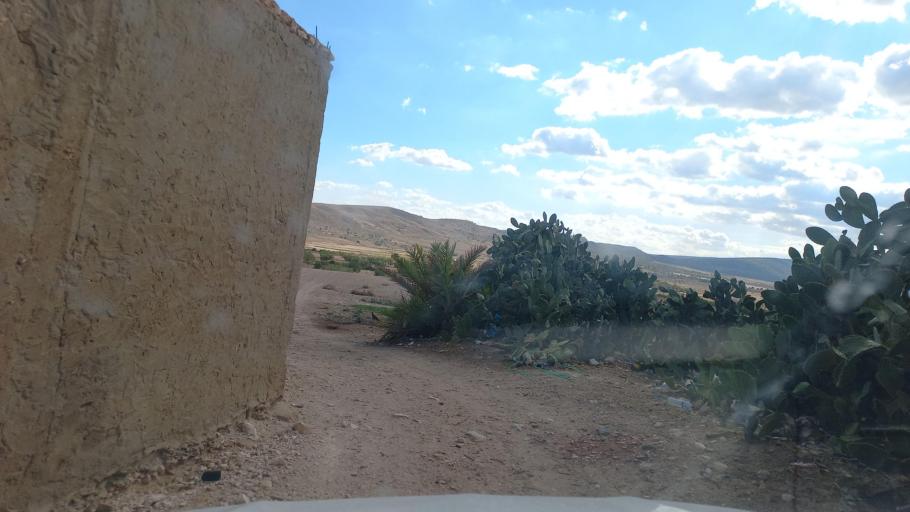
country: TN
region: Al Qasrayn
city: Sbiba
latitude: 35.4025
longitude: 9.0139
